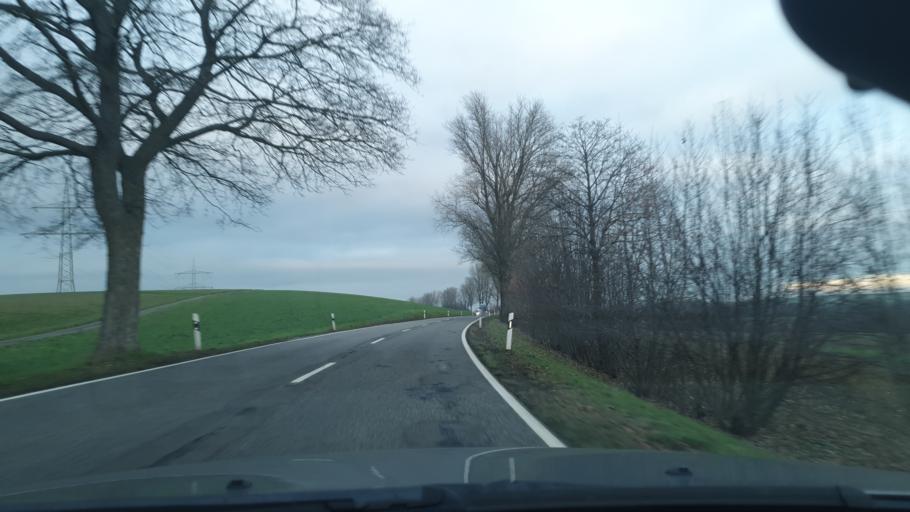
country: DE
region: Rheinland-Pfalz
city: Grossbundenbach
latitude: 49.3096
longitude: 7.3957
